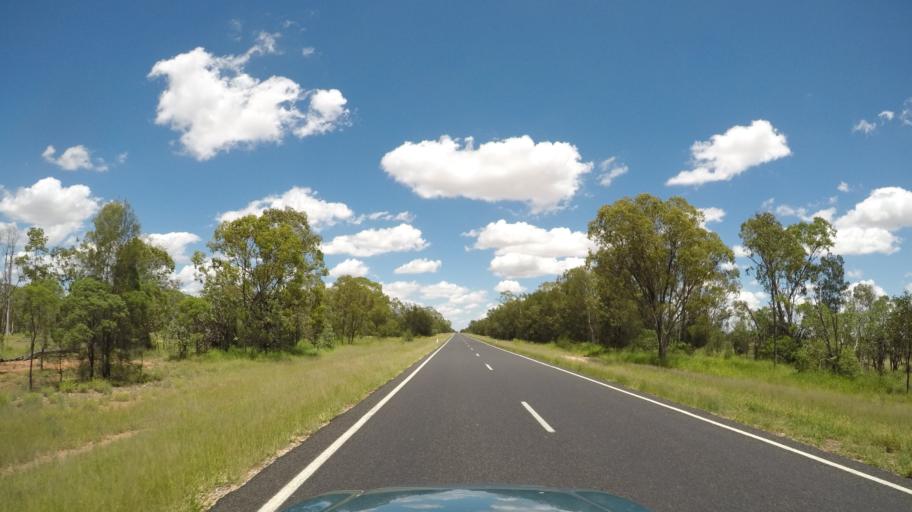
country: AU
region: Queensland
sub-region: Goondiwindi
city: Goondiwindi
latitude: -28.1669
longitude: 150.5996
